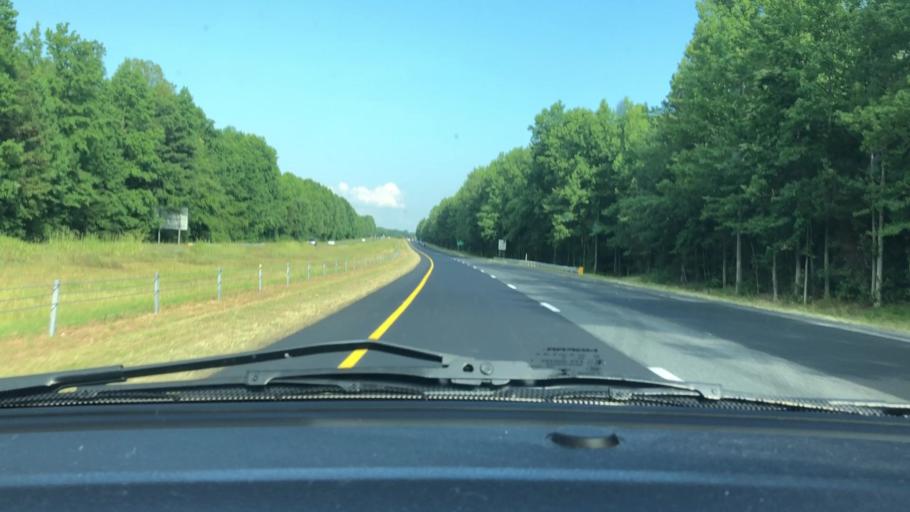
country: US
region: North Carolina
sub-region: Randolph County
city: Liberty
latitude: 35.8196
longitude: -79.5683
